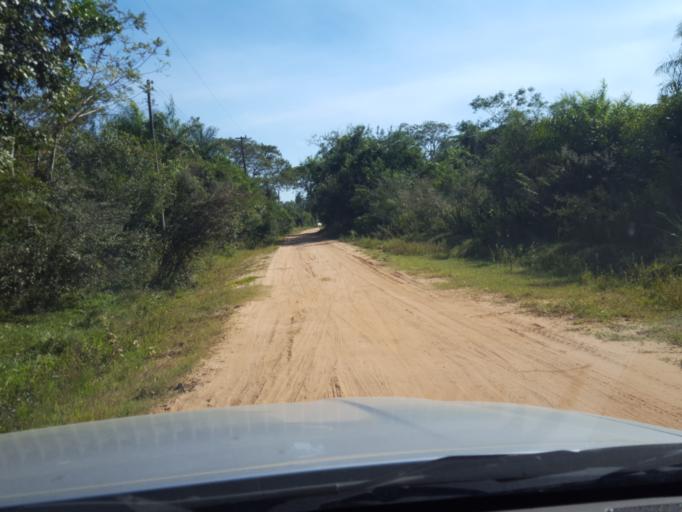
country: PY
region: Cordillera
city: Atyra
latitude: -25.2453
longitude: -57.1305
